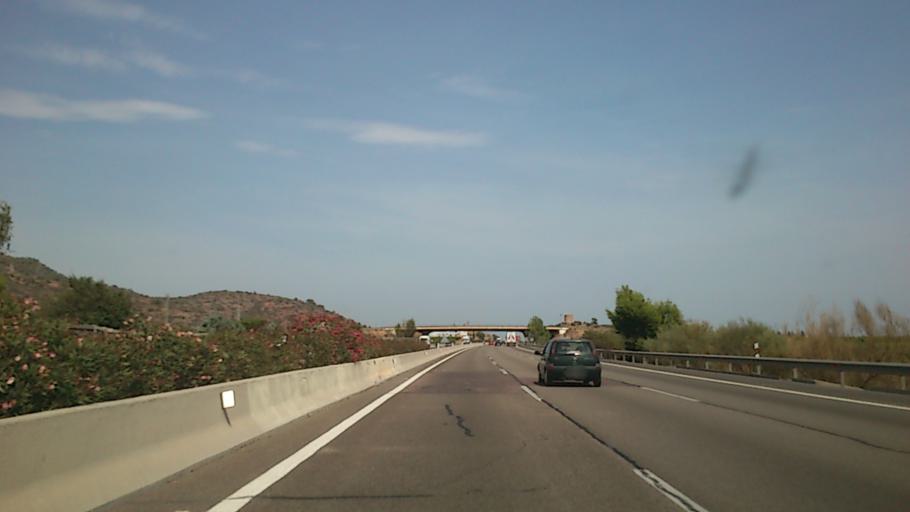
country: ES
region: Valencia
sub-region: Provincia de Valencia
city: Pucol
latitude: 39.6210
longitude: -0.3305
